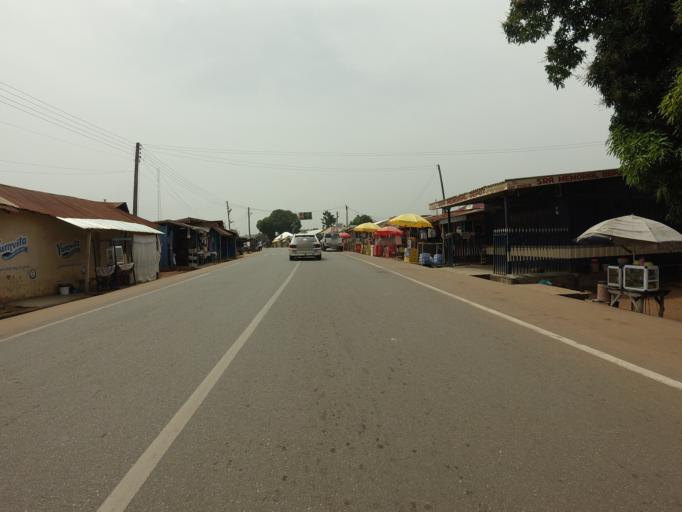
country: GH
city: Akropong
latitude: 6.0951
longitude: -0.0203
